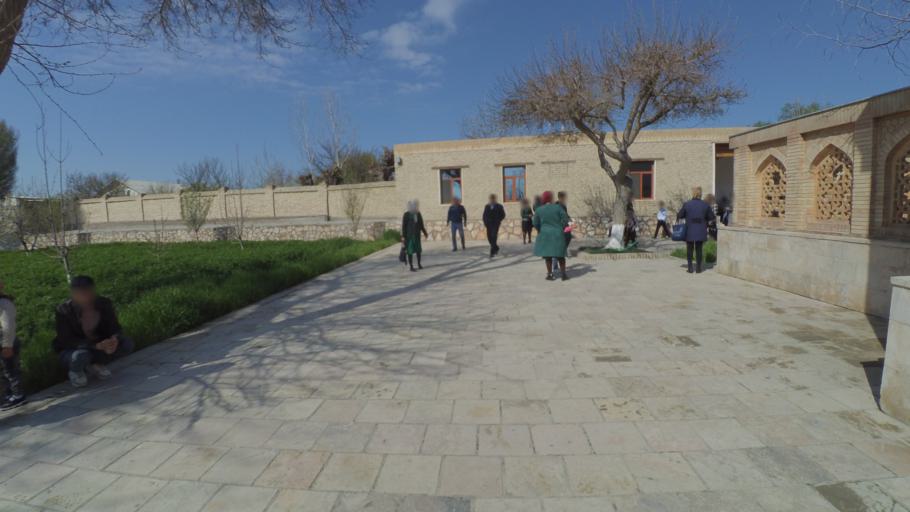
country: UZ
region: Bukhara
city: Kogon
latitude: 39.8053
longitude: 64.5401
